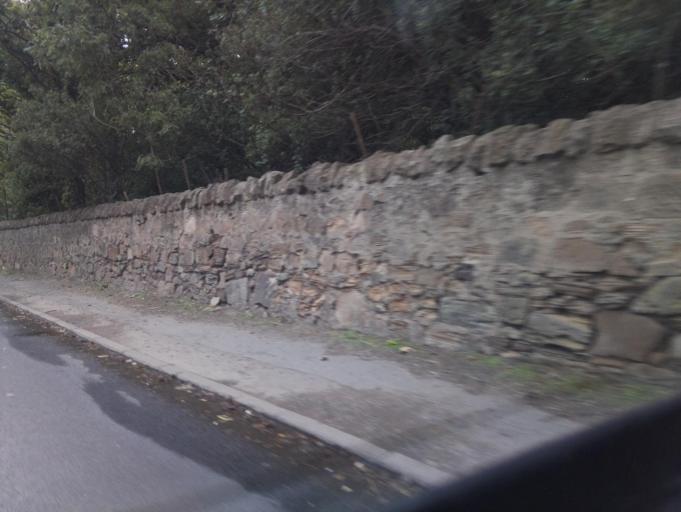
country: GB
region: Scotland
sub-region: East Lothian
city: Musselburgh
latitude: 55.9170
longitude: -3.0270
